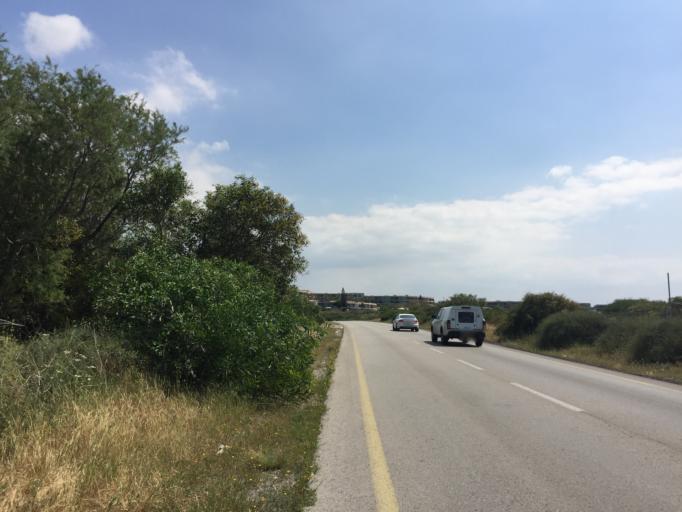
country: IL
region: Haifa
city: Qesarya
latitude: 32.4924
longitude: 34.8991
